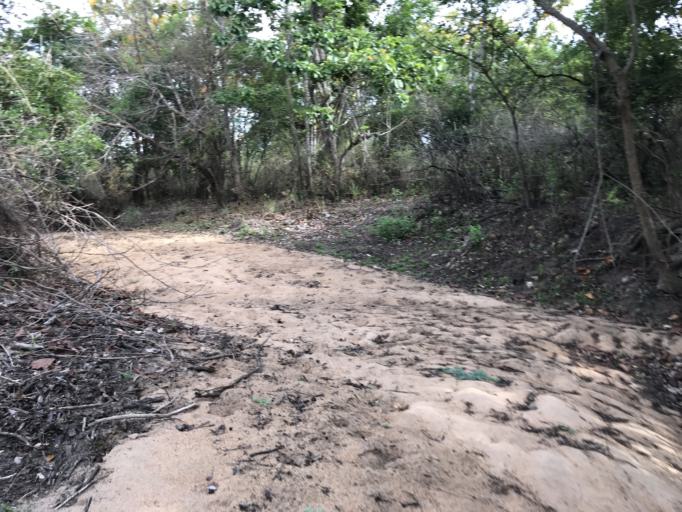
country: LK
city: Padaviya Divisional Secretariat
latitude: 9.0860
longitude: 80.8055
